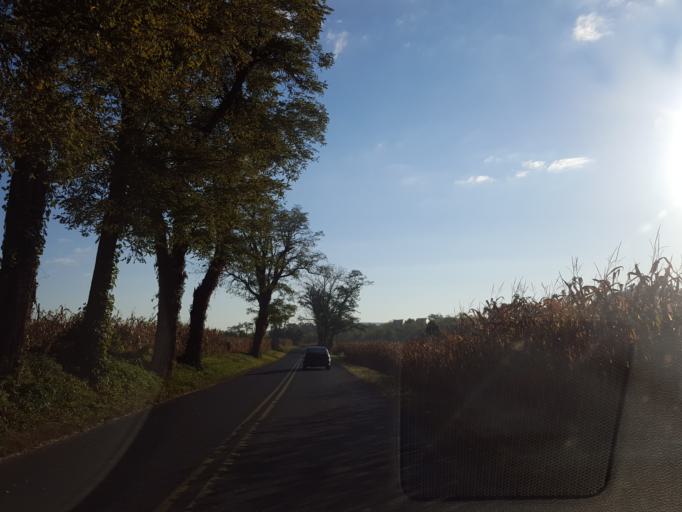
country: US
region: Pennsylvania
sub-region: York County
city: Stonybrook
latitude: 39.9528
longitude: -76.6312
